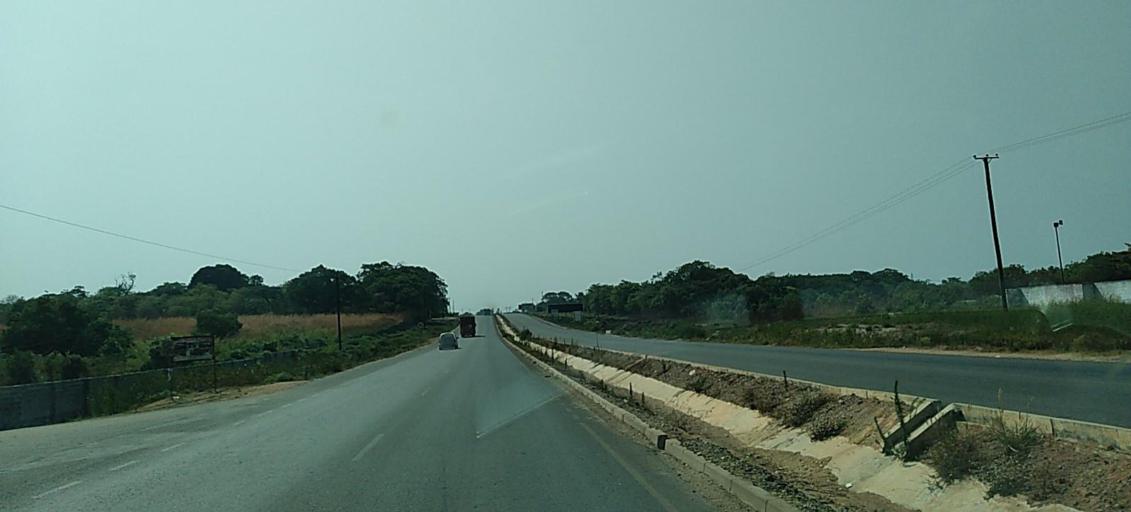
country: ZM
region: Copperbelt
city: Chingola
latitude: -12.5587
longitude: 27.8765
